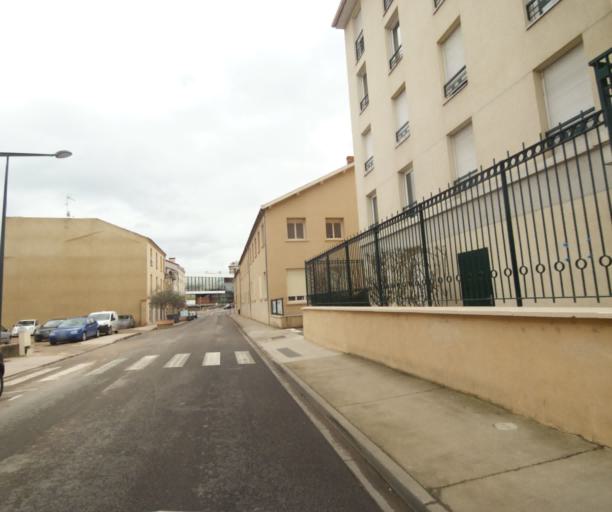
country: FR
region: Rhone-Alpes
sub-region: Departement de la Loire
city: Roanne
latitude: 46.0374
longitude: 4.0625
